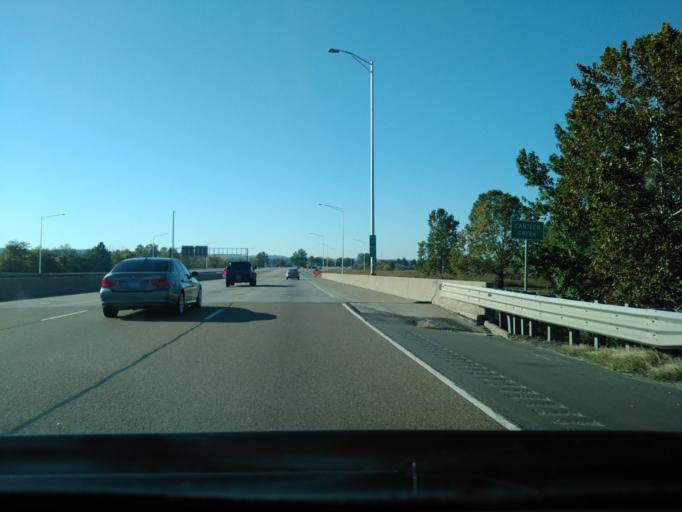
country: US
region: Illinois
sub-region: Saint Clair County
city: Caseyville
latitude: 38.6577
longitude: -90.0319
